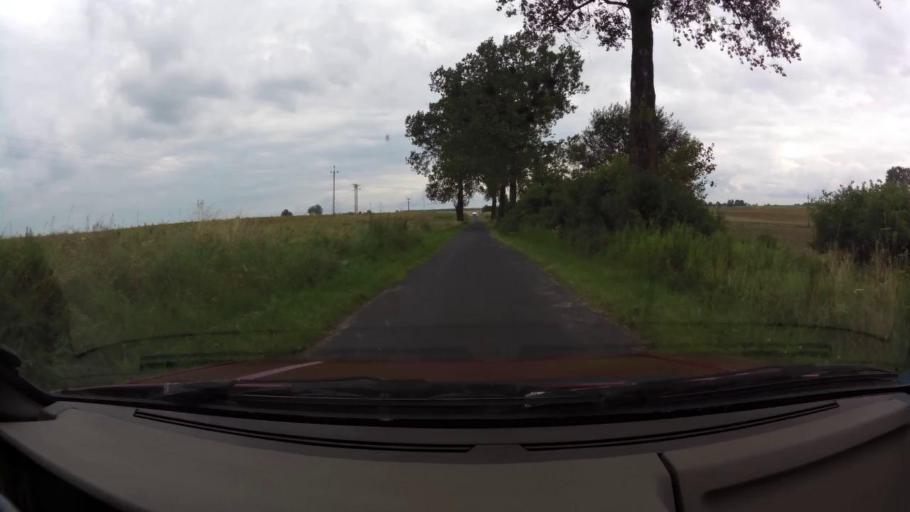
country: PL
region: West Pomeranian Voivodeship
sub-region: Powiat drawski
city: Drawsko Pomorskie
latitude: 53.5256
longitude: 15.7591
